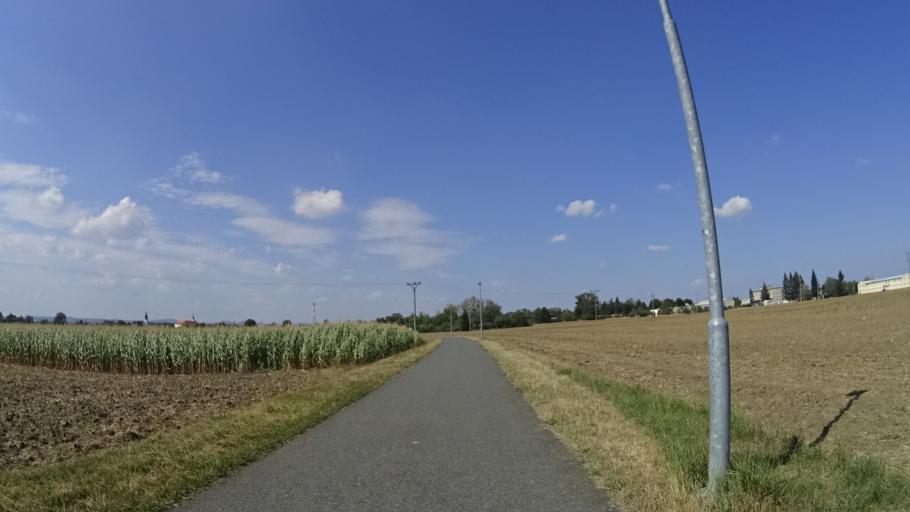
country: CZ
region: Zlin
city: Uhersky Ostroh
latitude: 48.9757
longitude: 17.3984
